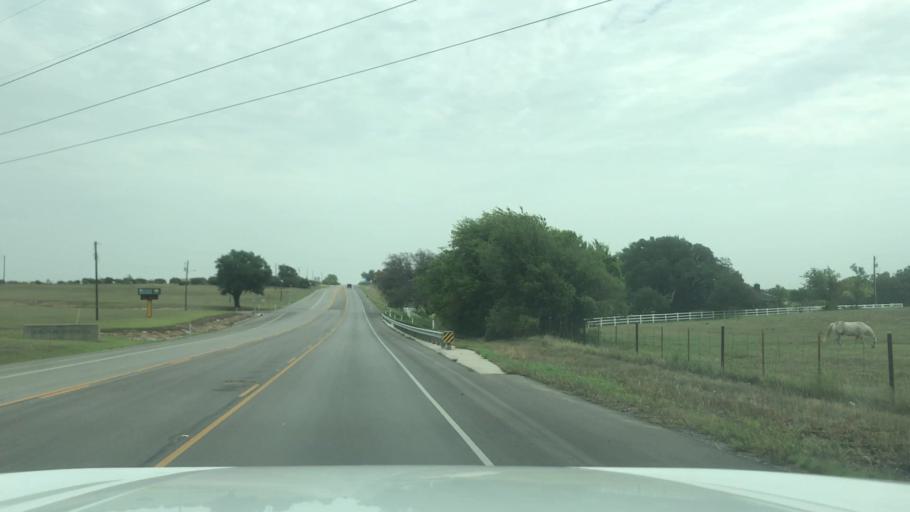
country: US
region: Texas
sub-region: Erath County
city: Dublin
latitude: 32.0849
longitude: -98.3214
